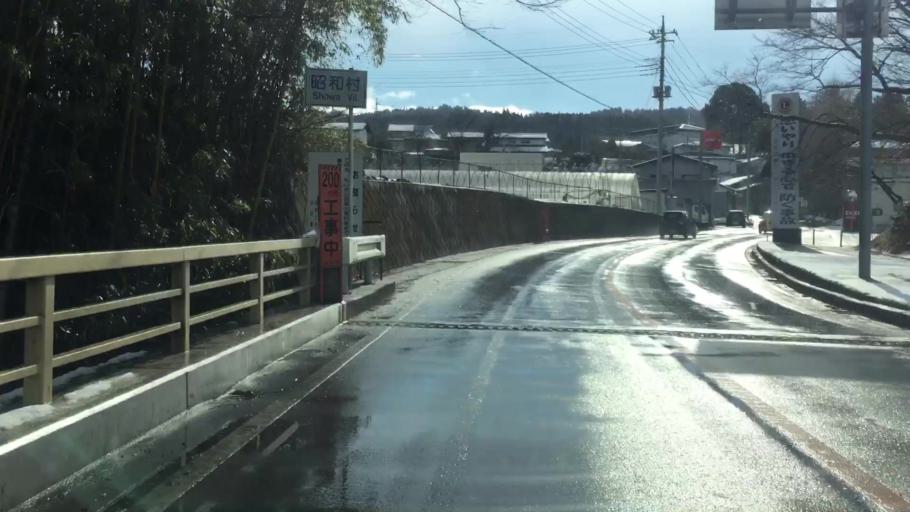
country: JP
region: Gunma
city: Numata
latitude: 36.6550
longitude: 139.0875
